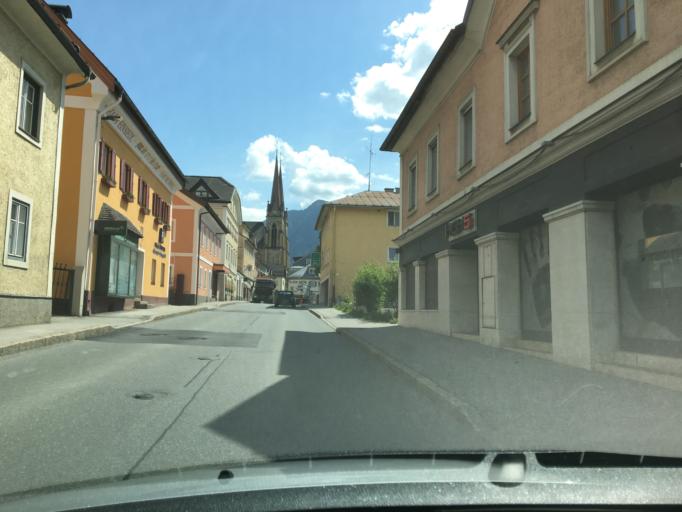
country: AT
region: Salzburg
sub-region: Politischer Bezirk Sankt Johann im Pongau
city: Sankt Johann im Pongau
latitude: 47.3510
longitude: 13.2050
